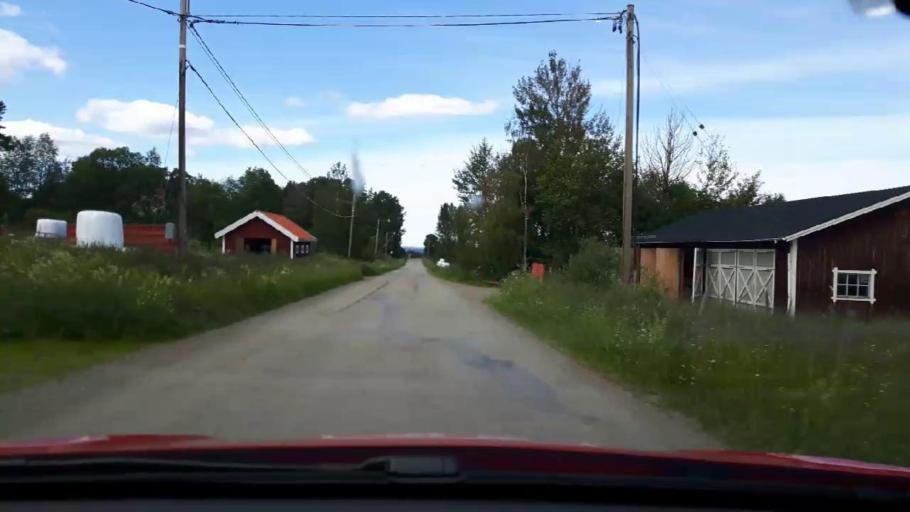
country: SE
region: Jaemtland
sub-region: Bergs Kommun
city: Hoverberg
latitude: 62.8214
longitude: 14.4605
